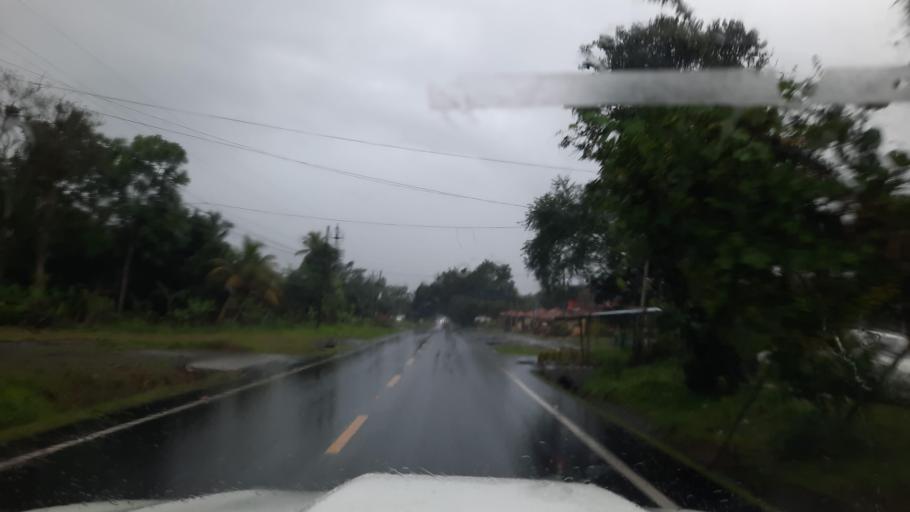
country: PA
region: Chiriqui
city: Sortova
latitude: 8.5757
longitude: -82.6357
